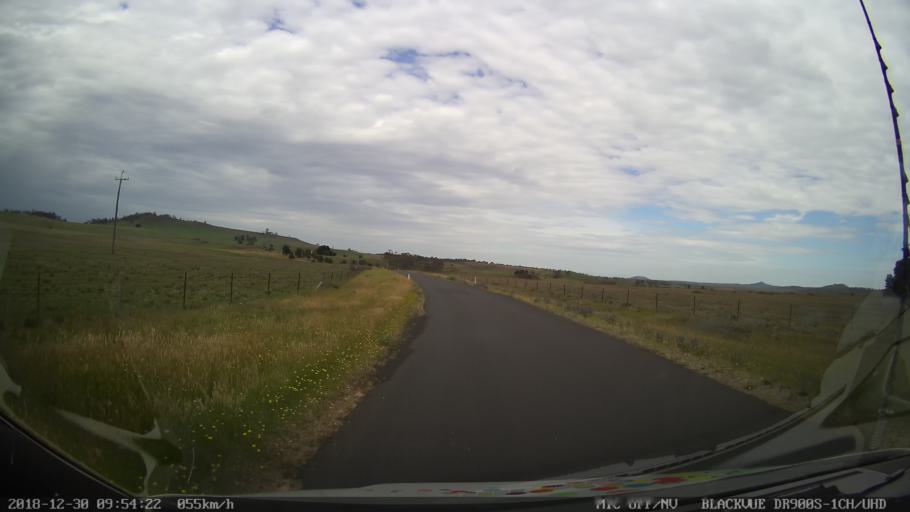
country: AU
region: New South Wales
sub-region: Cooma-Monaro
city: Cooma
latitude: -36.5184
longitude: 149.2783
